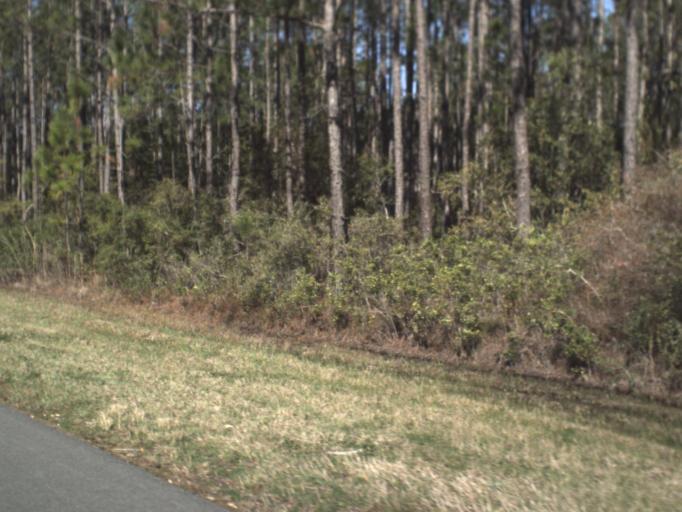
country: US
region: Florida
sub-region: Bay County
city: Callaway
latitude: 30.1527
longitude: -85.5144
